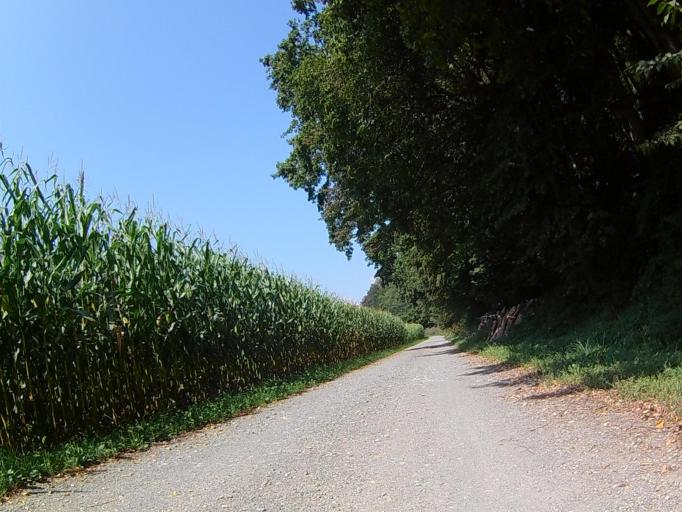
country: AT
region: Styria
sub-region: Politischer Bezirk Leibnitz
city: Oberhaag
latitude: 46.6883
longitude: 15.3466
